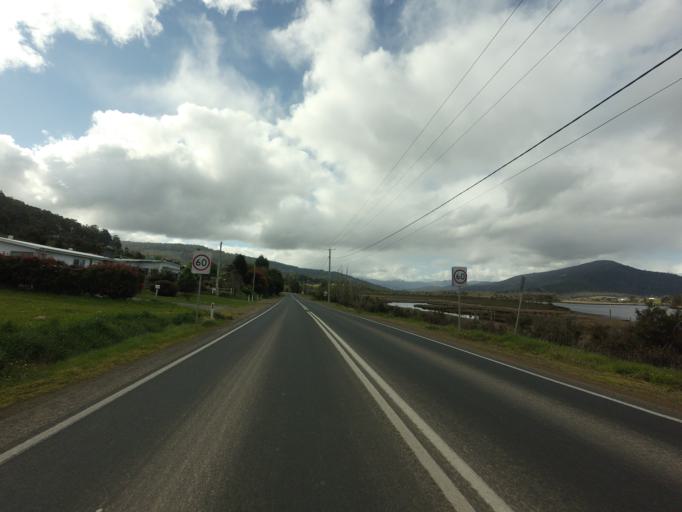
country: AU
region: Tasmania
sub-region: Huon Valley
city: Franklin
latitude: -43.0804
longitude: 147.0171
